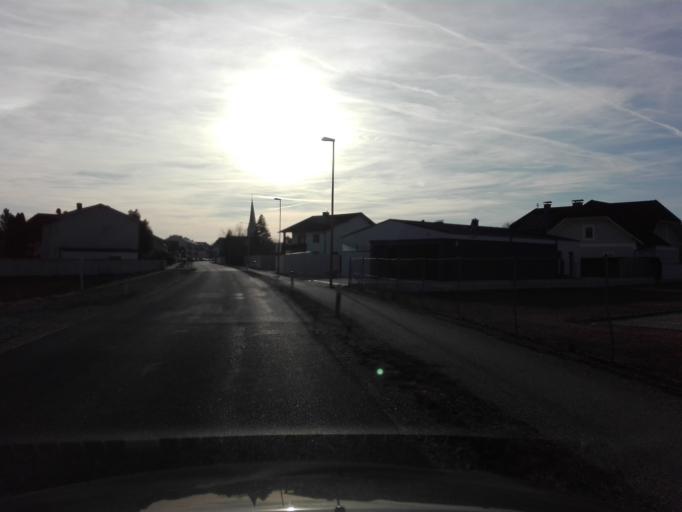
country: AT
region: Lower Austria
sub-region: Politischer Bezirk Amstetten
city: Sankt Valentin
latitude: 48.1781
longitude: 14.5385
